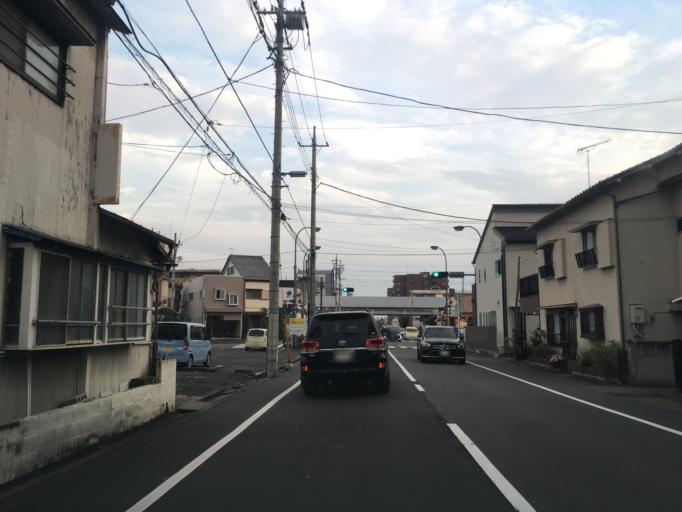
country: JP
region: Gunma
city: Maebashi-shi
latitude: 36.3850
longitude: 139.0764
